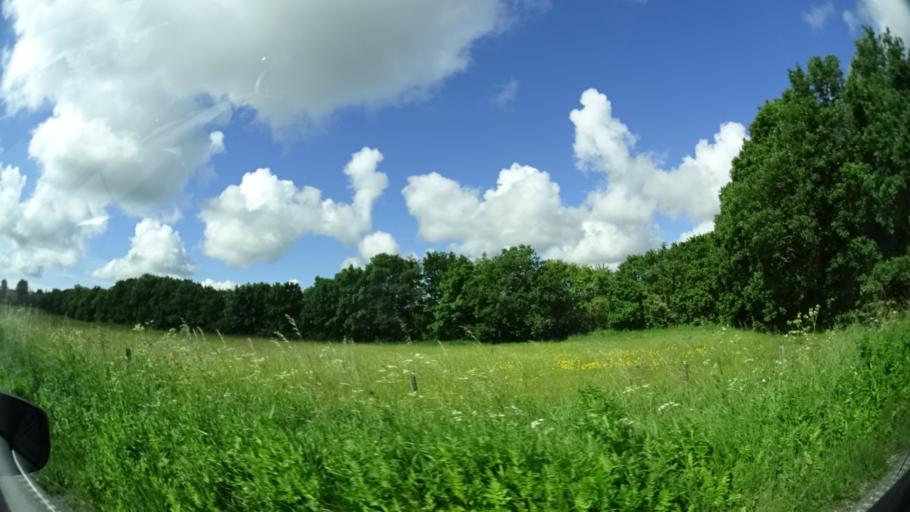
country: DK
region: Central Jutland
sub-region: Syddjurs Kommune
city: Ronde
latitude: 56.2805
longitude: 10.5911
